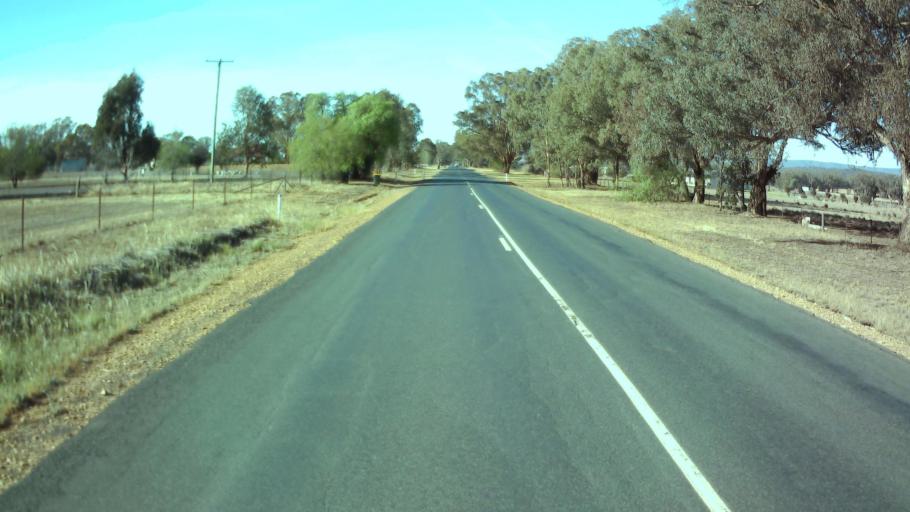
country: AU
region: New South Wales
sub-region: Weddin
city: Grenfell
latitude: -33.9086
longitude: 148.1457
